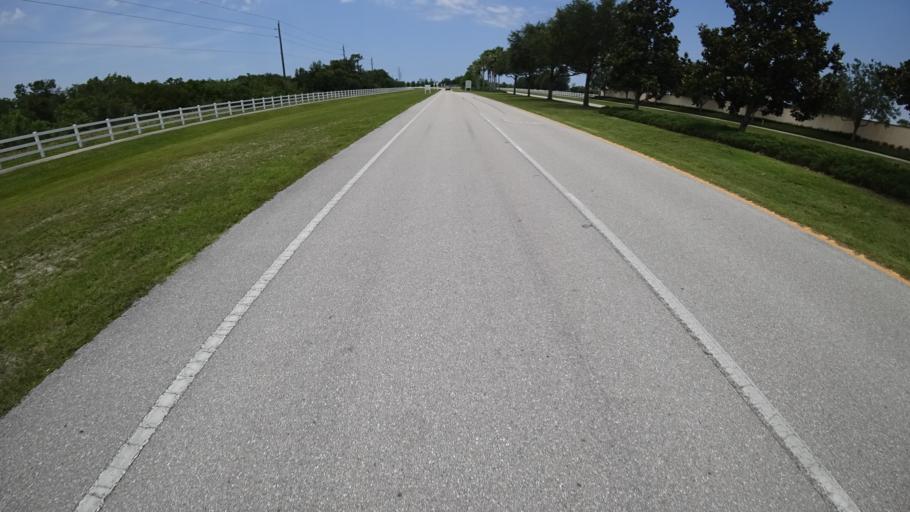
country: US
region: Florida
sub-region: Sarasota County
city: The Meadows
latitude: 27.3880
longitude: -82.3855
